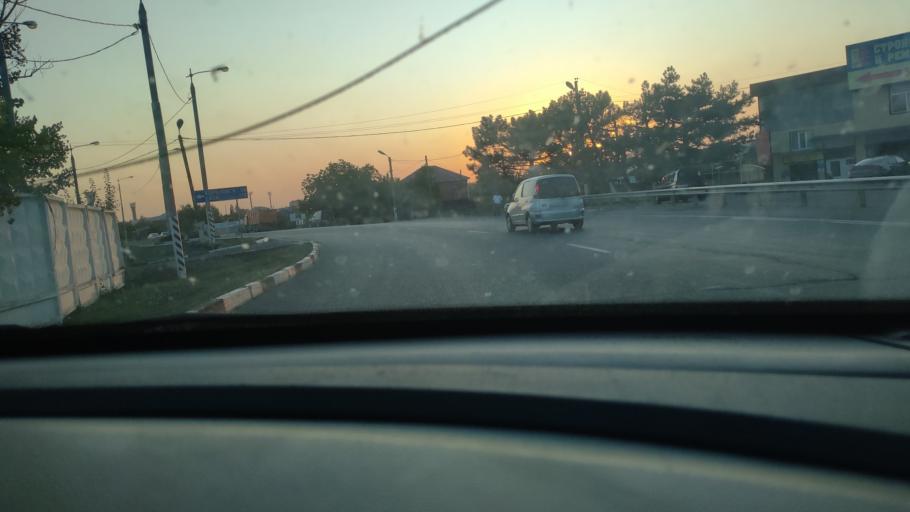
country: RU
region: Krasnodarskiy
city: Timashevsk
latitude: 45.6005
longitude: 38.9302
